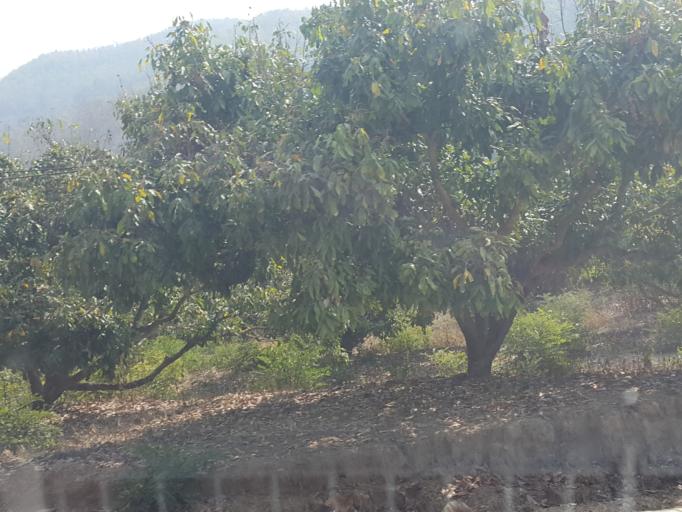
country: TH
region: Chiang Mai
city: Hang Dong
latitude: 18.7369
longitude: 98.8608
